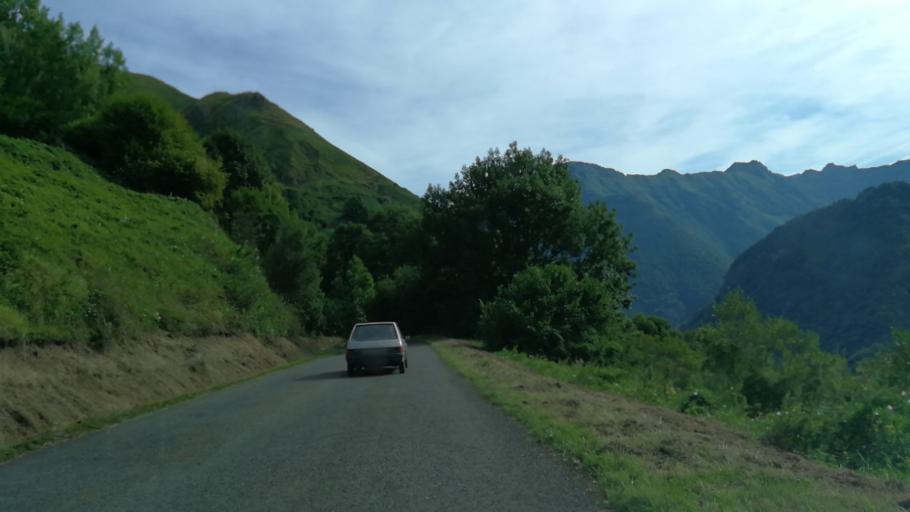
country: FR
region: Aquitaine
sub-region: Departement des Pyrenees-Atlantiques
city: Arette
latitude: 42.9324
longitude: -0.6332
